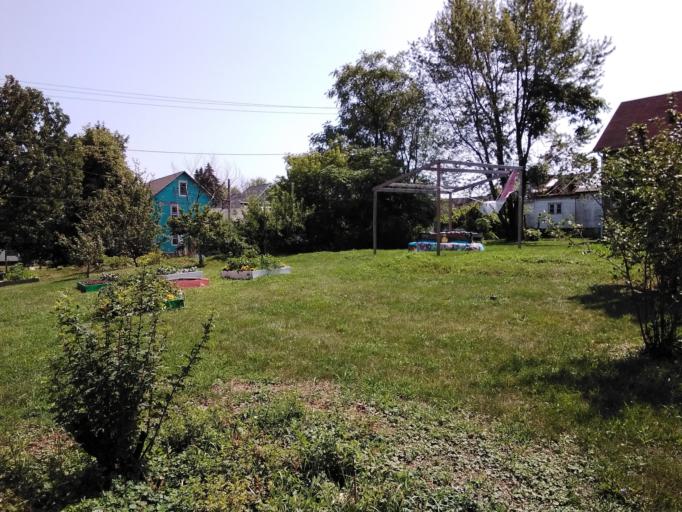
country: US
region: Wisconsin
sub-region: Milwaukee County
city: Milwaukee
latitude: 43.0657
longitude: -87.9077
